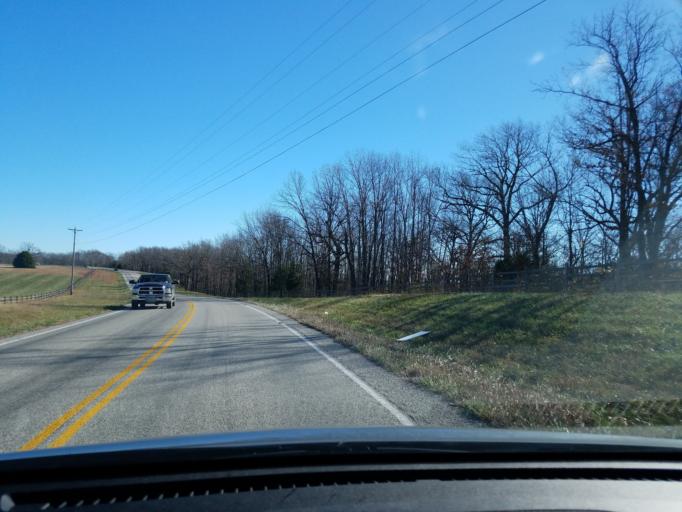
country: US
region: Missouri
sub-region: Taney County
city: Hollister
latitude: 36.5206
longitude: -93.2679
